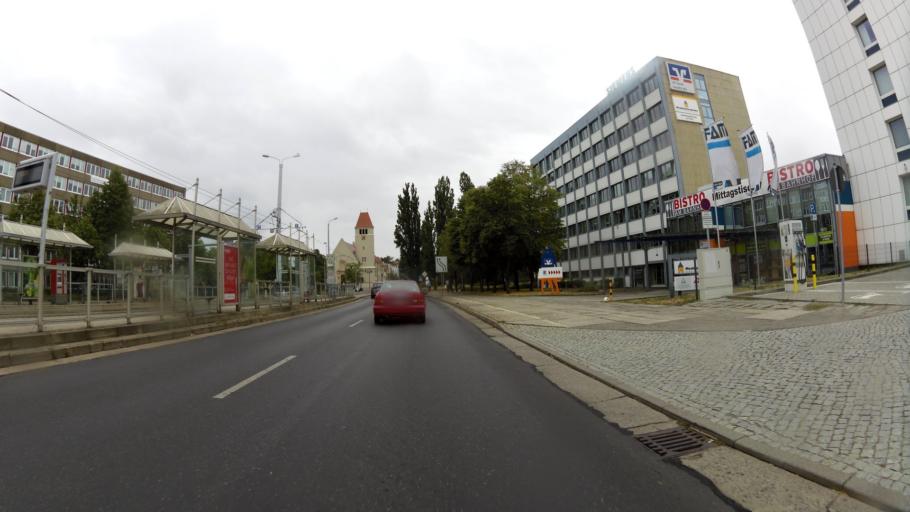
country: DE
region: Brandenburg
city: Cottbus
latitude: 51.7489
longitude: 14.3282
